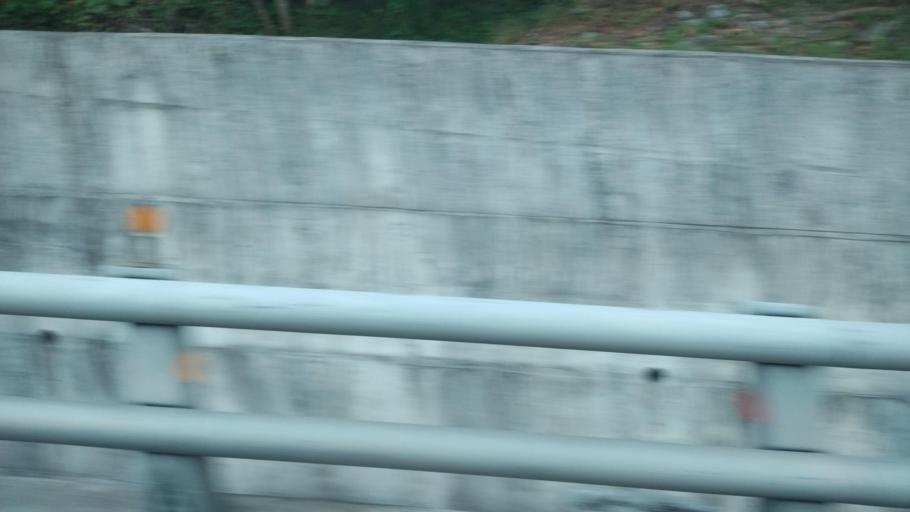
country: TW
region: Taiwan
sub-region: Hualien
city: Hualian
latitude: 24.2353
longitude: 121.7083
